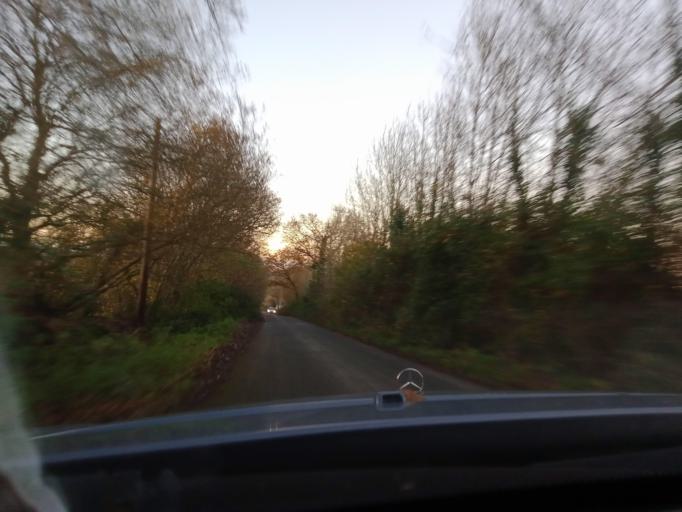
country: IE
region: Leinster
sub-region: Kilkenny
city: Thomastown
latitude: 52.4847
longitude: -7.1008
